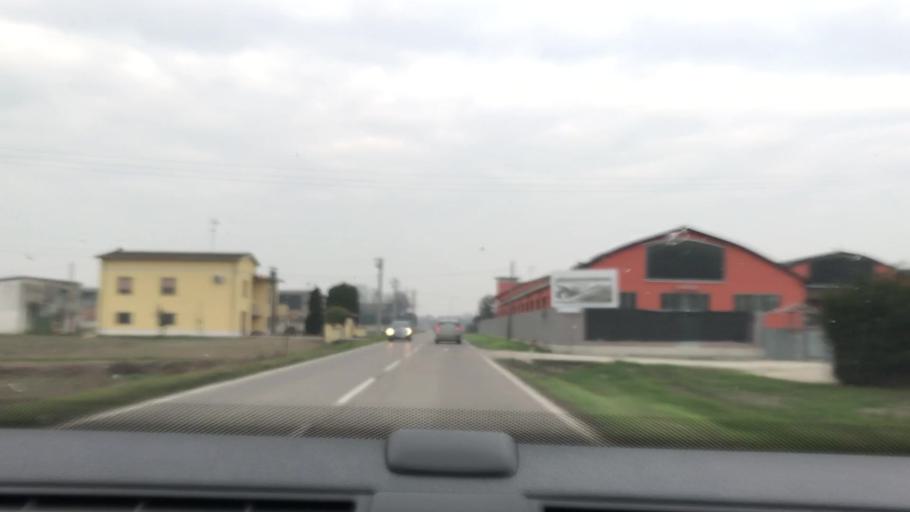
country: IT
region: Lombardy
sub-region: Provincia di Mantova
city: Dosolo
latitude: 44.9435
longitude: 10.6266
